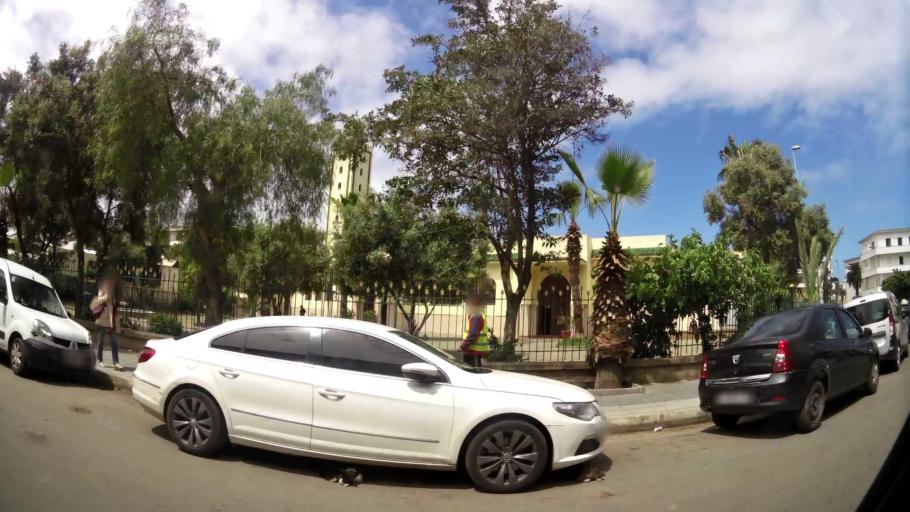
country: MA
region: Grand Casablanca
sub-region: Casablanca
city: Casablanca
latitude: 33.5937
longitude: -7.6390
